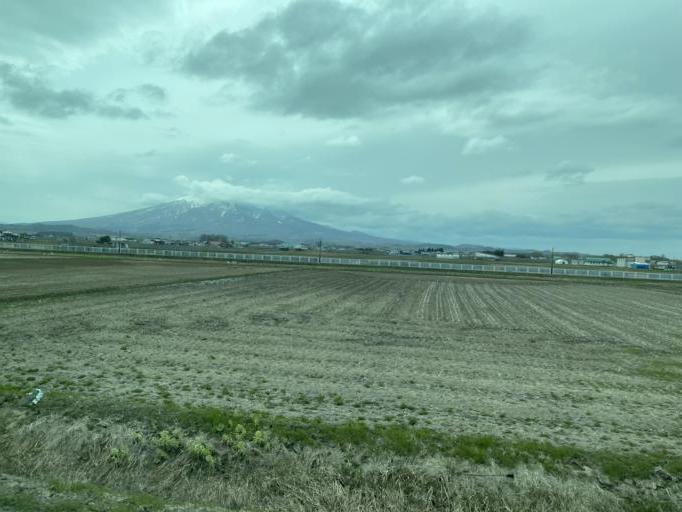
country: JP
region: Aomori
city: Goshogawara
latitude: 40.7419
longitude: 140.4354
